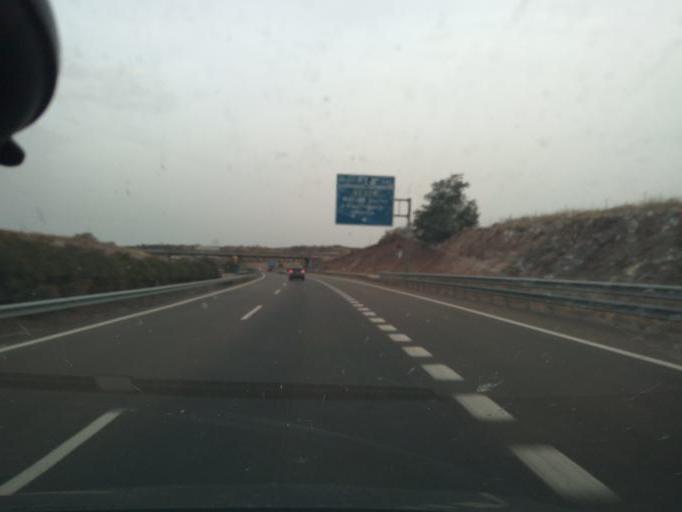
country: ES
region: Extremadura
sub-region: Provincia de Badajoz
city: Merida
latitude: 38.9429
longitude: -6.3514
